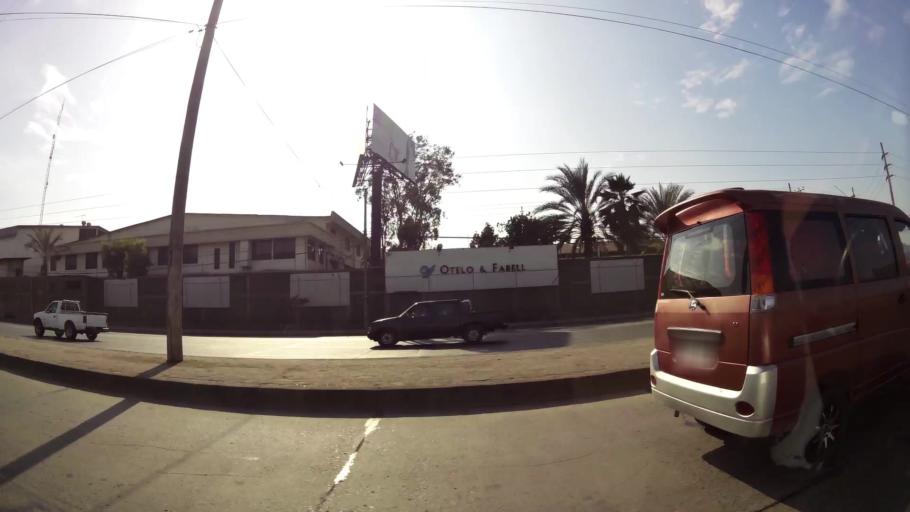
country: EC
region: Guayas
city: Santa Lucia
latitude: -2.0723
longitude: -79.9415
